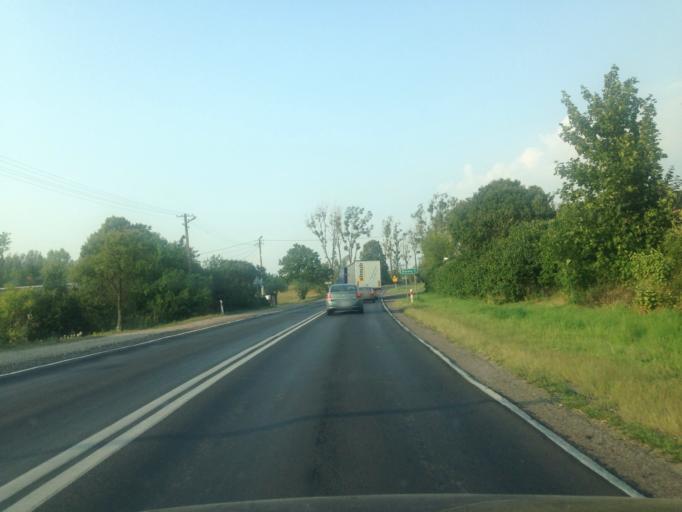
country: PL
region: Kujawsko-Pomorskie
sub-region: Powiat wloclawski
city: Fabianki
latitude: 52.7898
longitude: 19.1183
